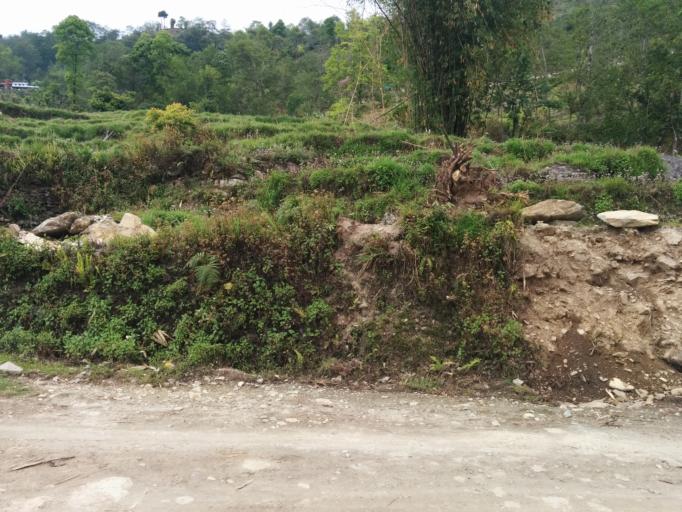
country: NP
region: Western Region
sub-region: Gandaki Zone
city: Pokhara
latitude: 28.2836
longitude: 83.8362
